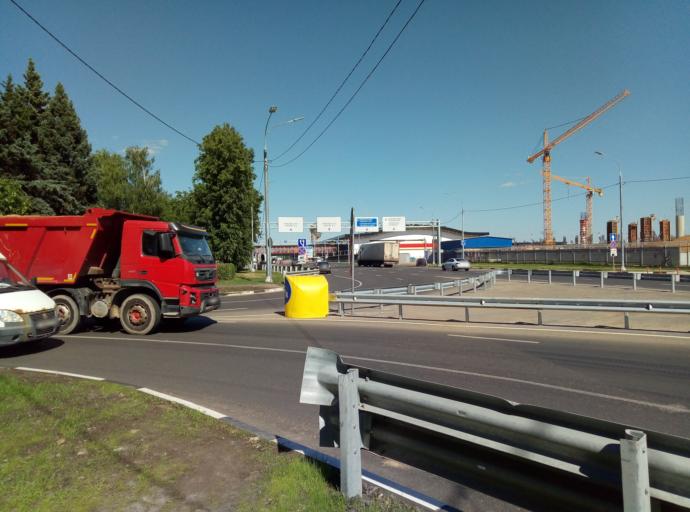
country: RU
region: Moskovskaya
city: Novopodrezkovo
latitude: 55.9811
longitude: 37.4057
